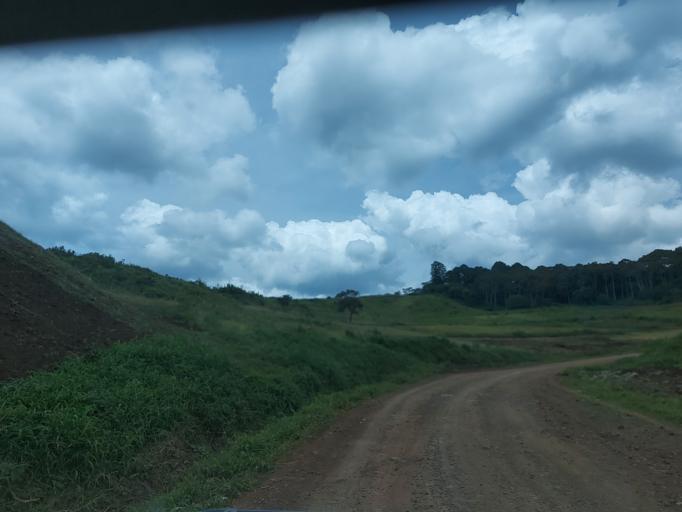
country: CD
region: South Kivu
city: Kabare
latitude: -2.3182
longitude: 28.7617
